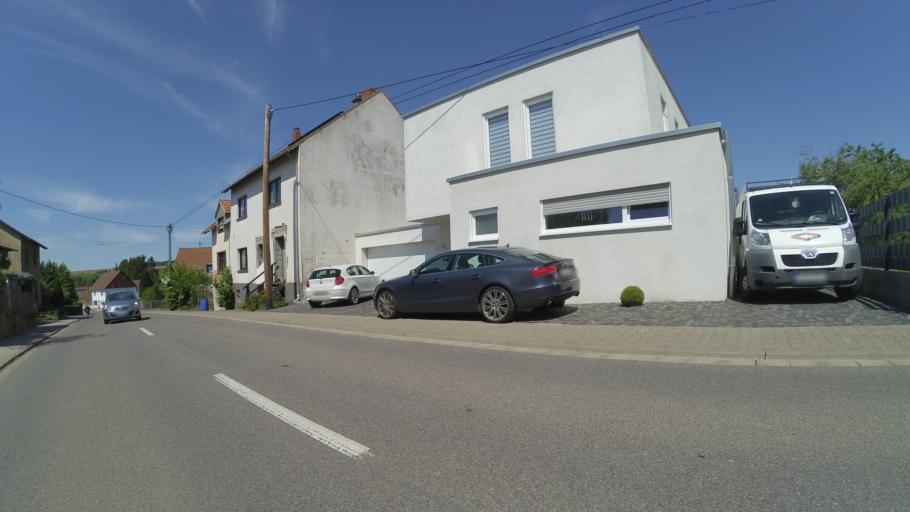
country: DE
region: Saarland
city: Heusweiler
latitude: 49.3321
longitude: 6.9132
